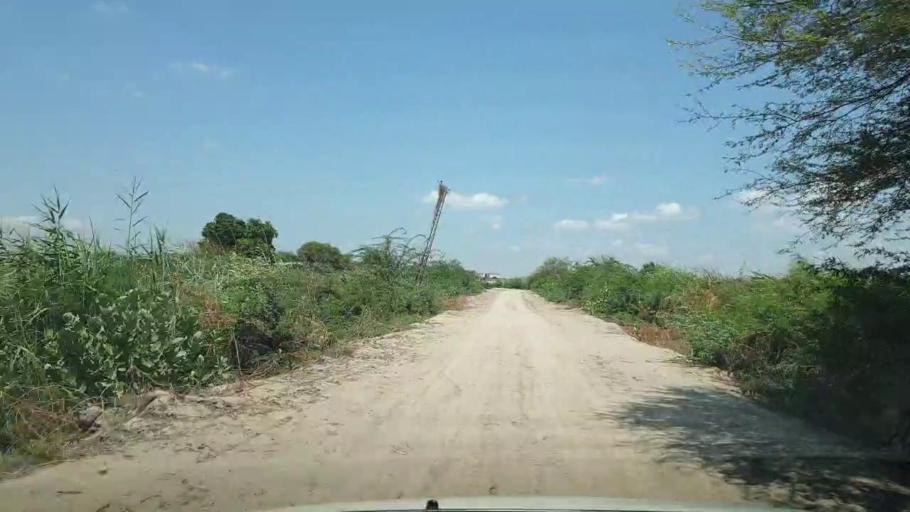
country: PK
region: Sindh
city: Sanghar
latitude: 26.1082
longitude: 69.0131
